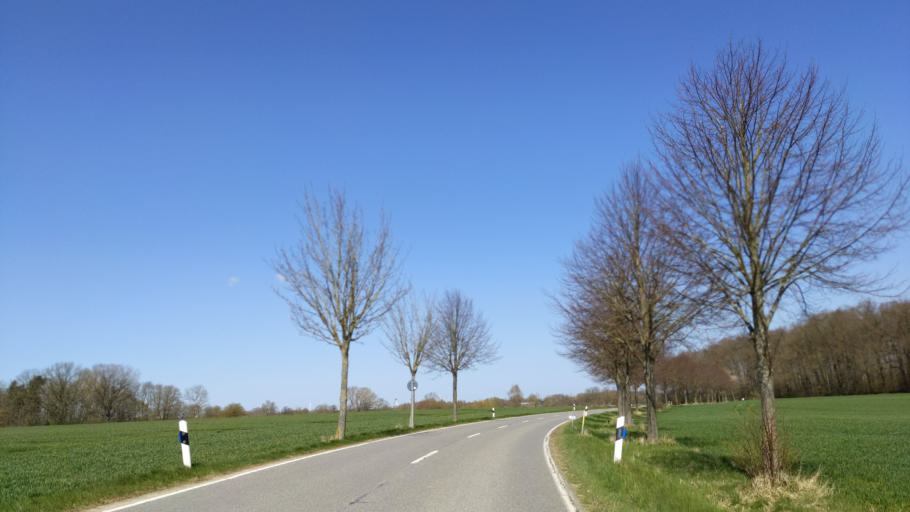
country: DE
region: Schleswig-Holstein
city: Susel
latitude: 54.0165
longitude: 10.6571
